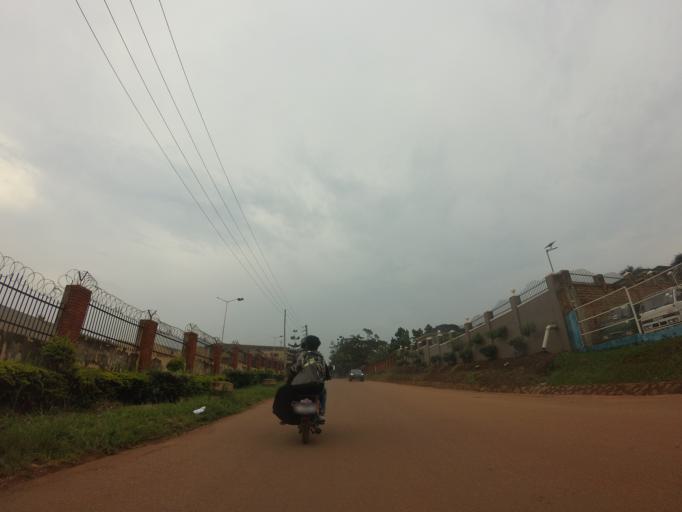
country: UG
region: Central Region
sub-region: Wakiso District
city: Kireka
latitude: 0.3418
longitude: 32.6256
